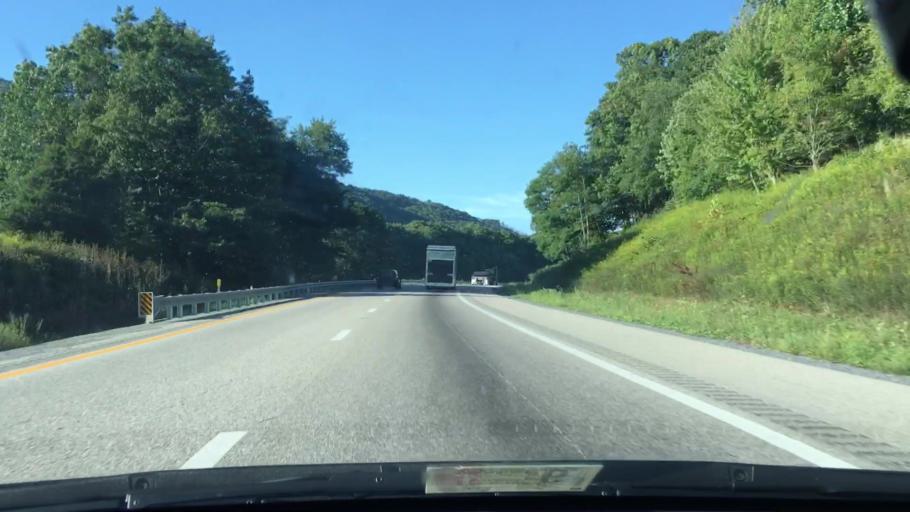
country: US
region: Virginia
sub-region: City of Lexington
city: Lexington
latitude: 37.8668
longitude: -79.6241
